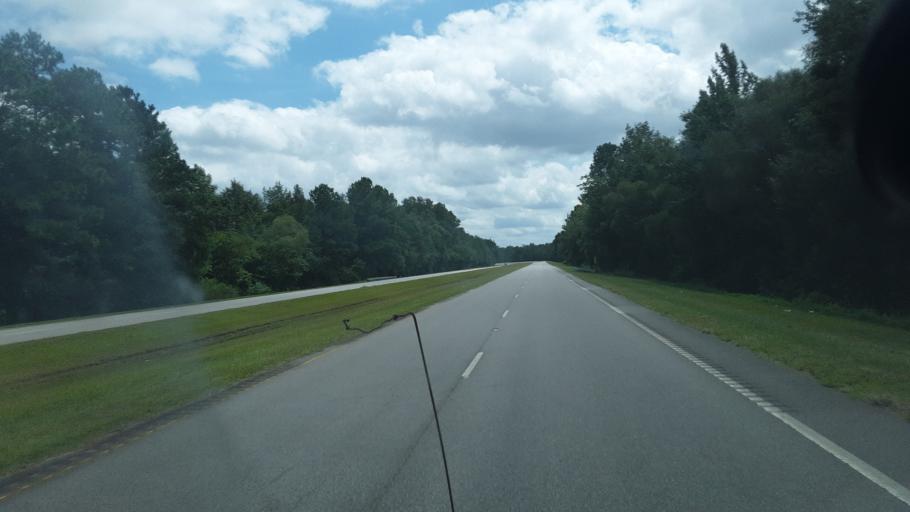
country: US
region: North Carolina
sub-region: Columbus County
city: Tabor City
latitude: 34.1268
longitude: -78.9859
